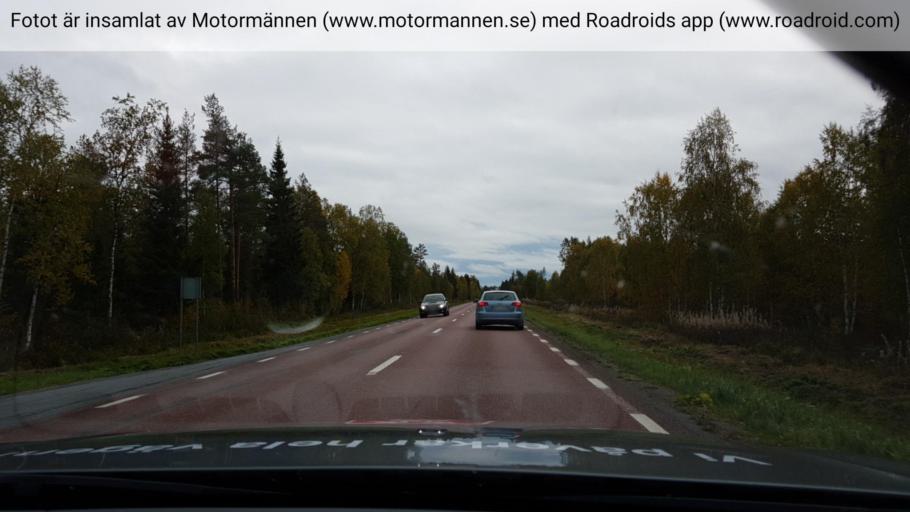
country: SE
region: Jaemtland
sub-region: Stroemsunds Kommun
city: Stroemsund
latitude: 63.7569
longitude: 15.4989
